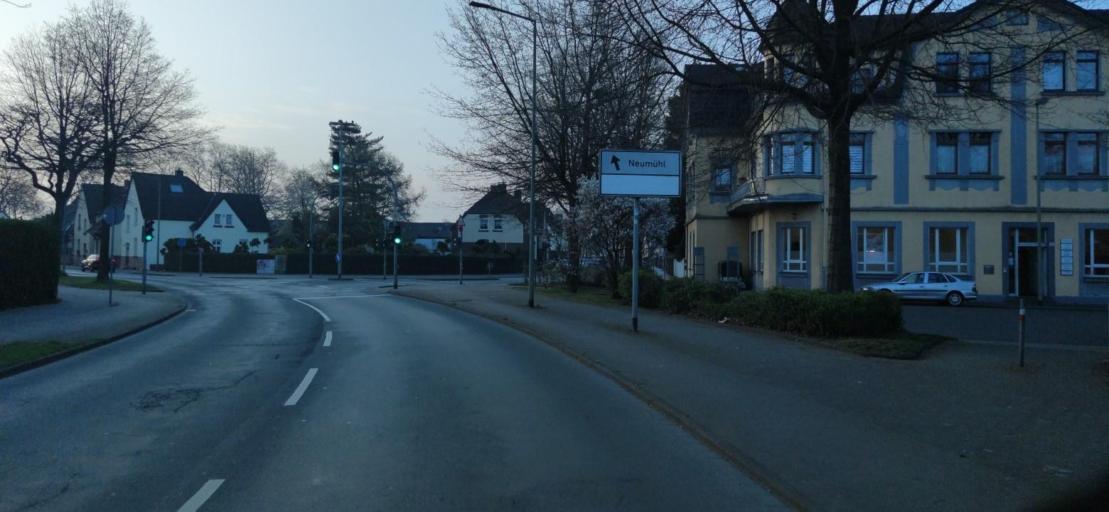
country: DE
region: North Rhine-Westphalia
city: Meiderich
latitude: 51.4977
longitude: 6.7868
